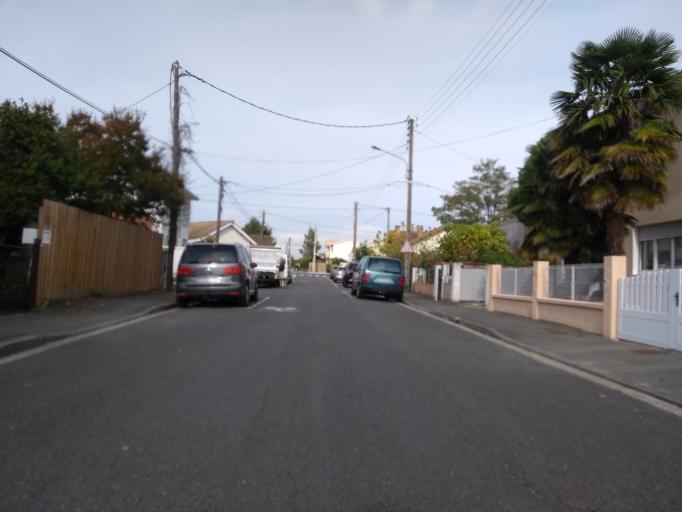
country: FR
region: Aquitaine
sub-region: Departement de la Gironde
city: Talence
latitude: 44.8073
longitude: -0.6168
